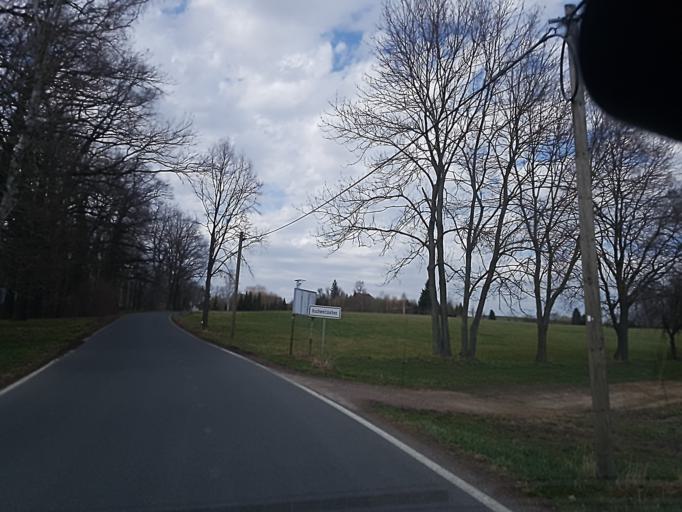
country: DE
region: Saxony
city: Grossweitzschen
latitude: 51.1408
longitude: 13.0357
